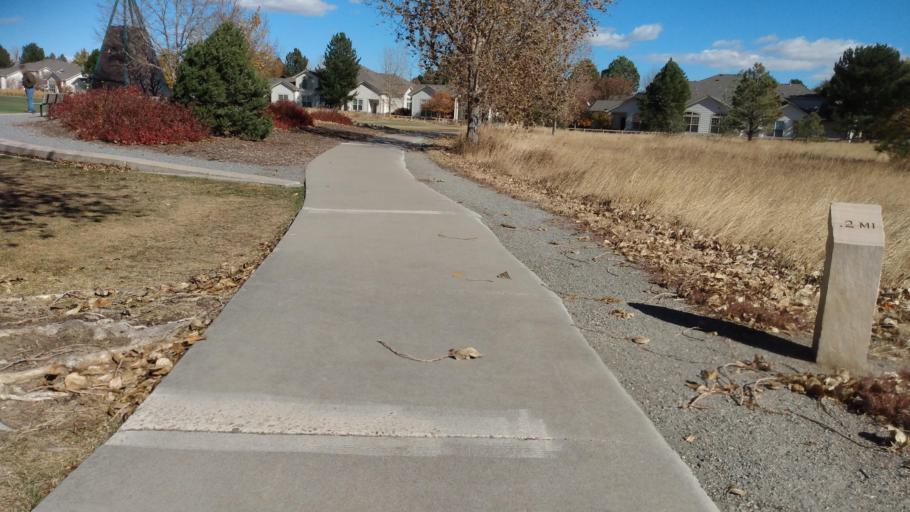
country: US
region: Colorado
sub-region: Boulder County
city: Lafayette
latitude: 39.9689
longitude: -105.0938
